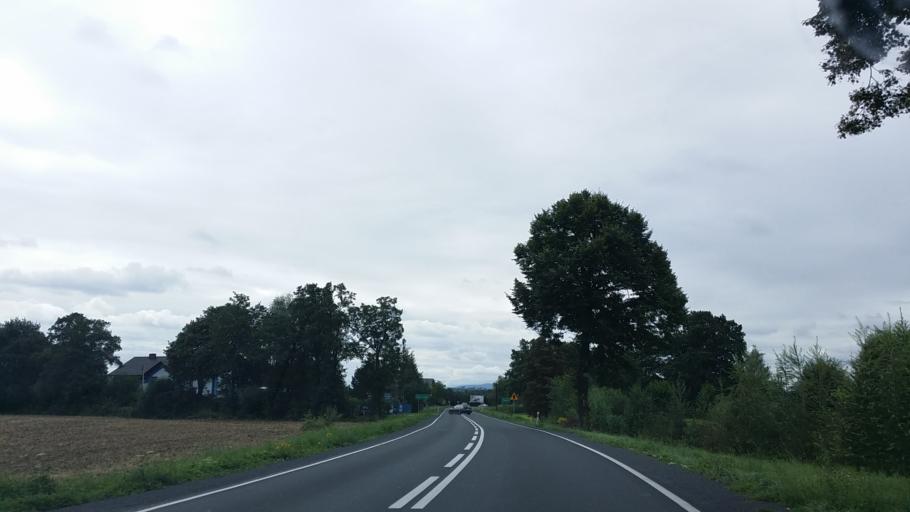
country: PL
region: Lesser Poland Voivodeship
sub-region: Powiat oswiecimski
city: Zator
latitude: 49.9710
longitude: 19.4406
